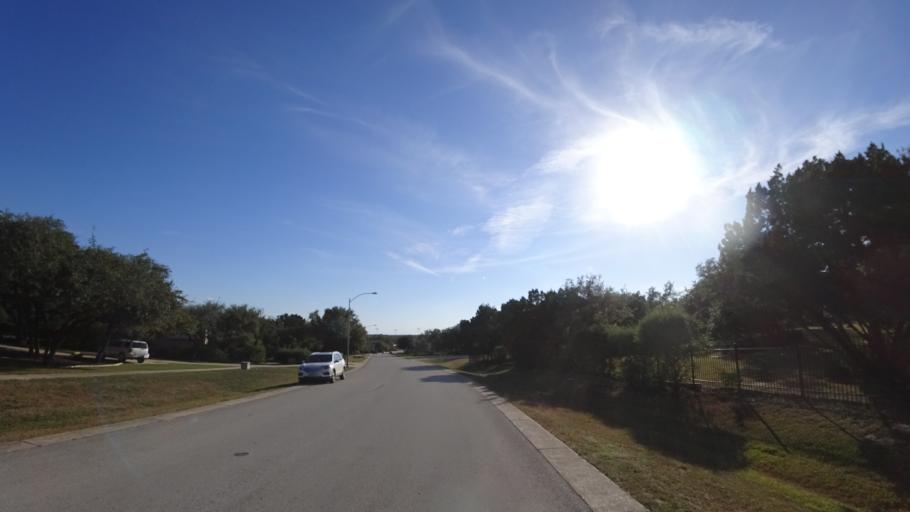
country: US
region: Texas
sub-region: Travis County
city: Barton Creek
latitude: 30.2582
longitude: -97.8440
